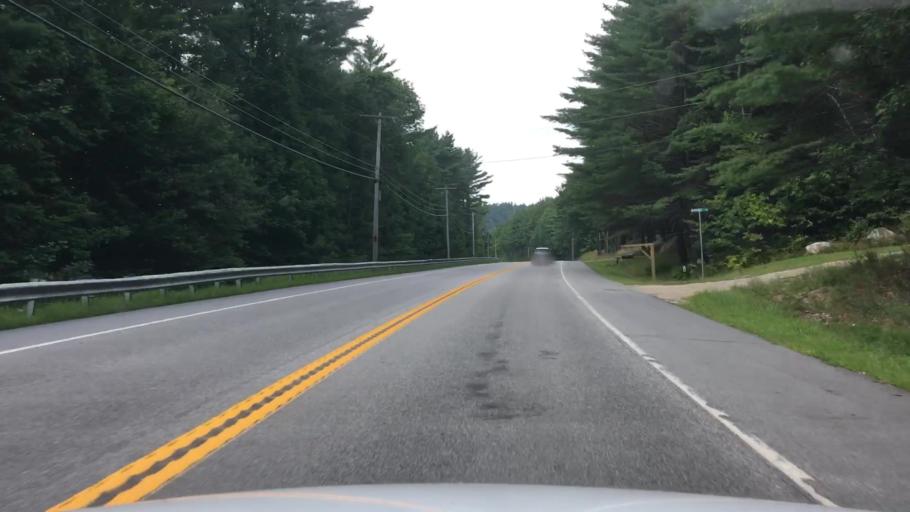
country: US
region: Maine
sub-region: Oxford County
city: Rumford
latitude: 44.5095
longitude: -70.6066
